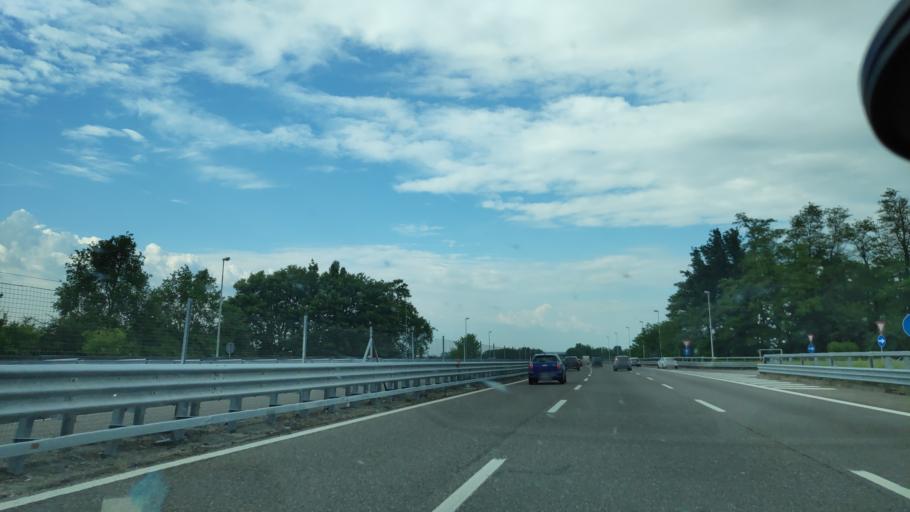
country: IT
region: Lombardy
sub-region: Provincia di Pavia
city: Gropello Cairoli
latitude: 45.1492
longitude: 8.9922
